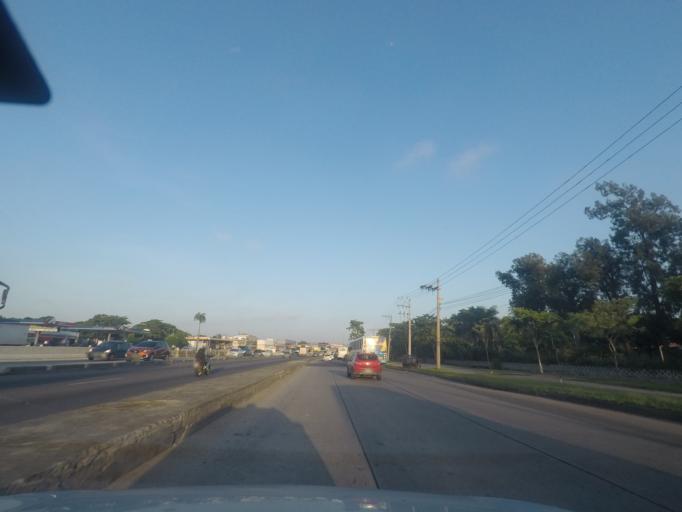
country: BR
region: Rio de Janeiro
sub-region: Duque De Caxias
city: Duque de Caxias
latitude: -22.8311
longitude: -43.2685
